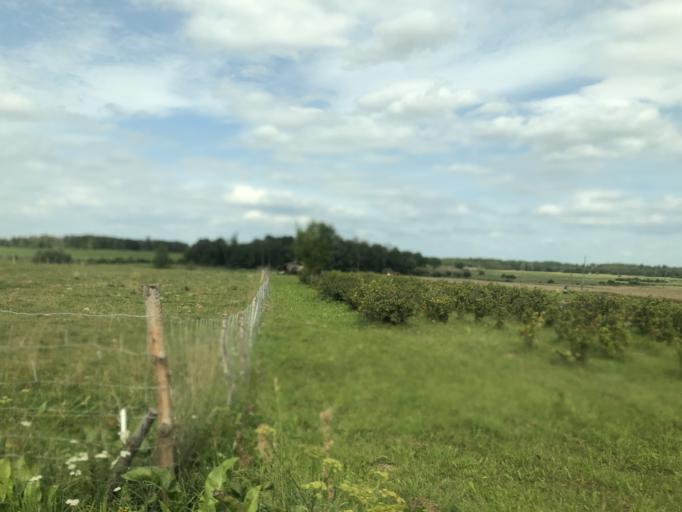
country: LV
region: Vecumnieki
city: Vecumnieki
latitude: 56.4598
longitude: 24.6063
